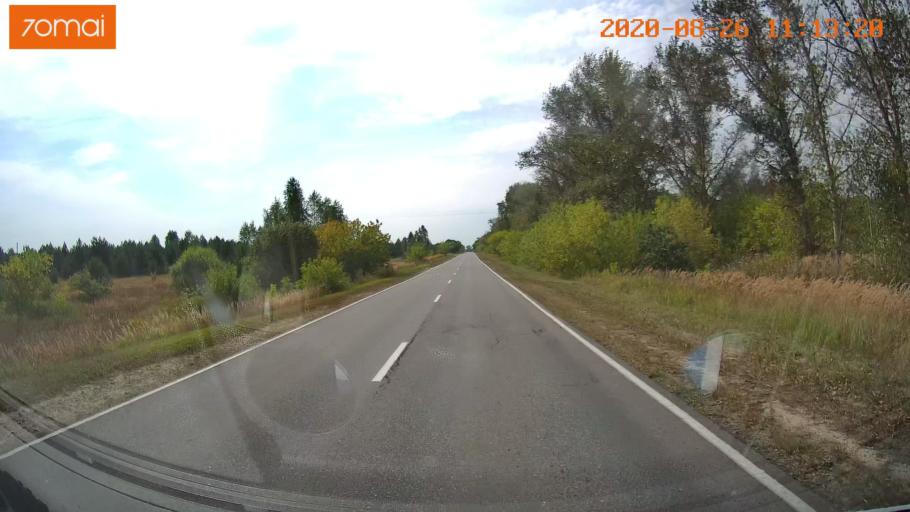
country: RU
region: Rjazan
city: Izhevskoye
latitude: 54.4591
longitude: 41.1212
